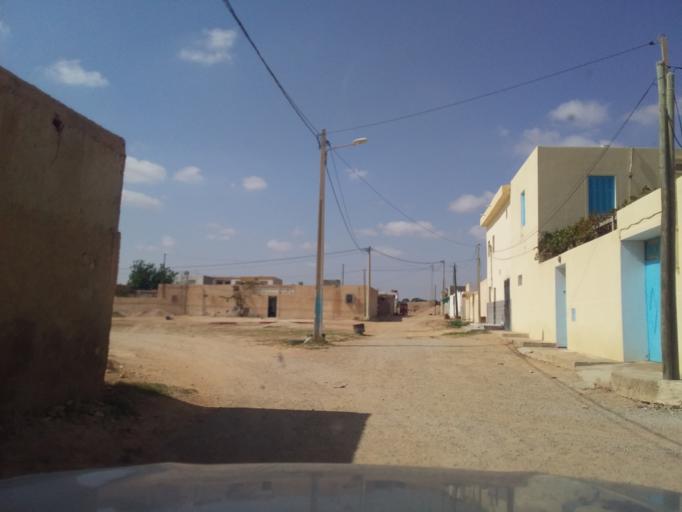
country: TN
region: Madanin
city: Medenine
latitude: 33.5822
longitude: 10.3224
